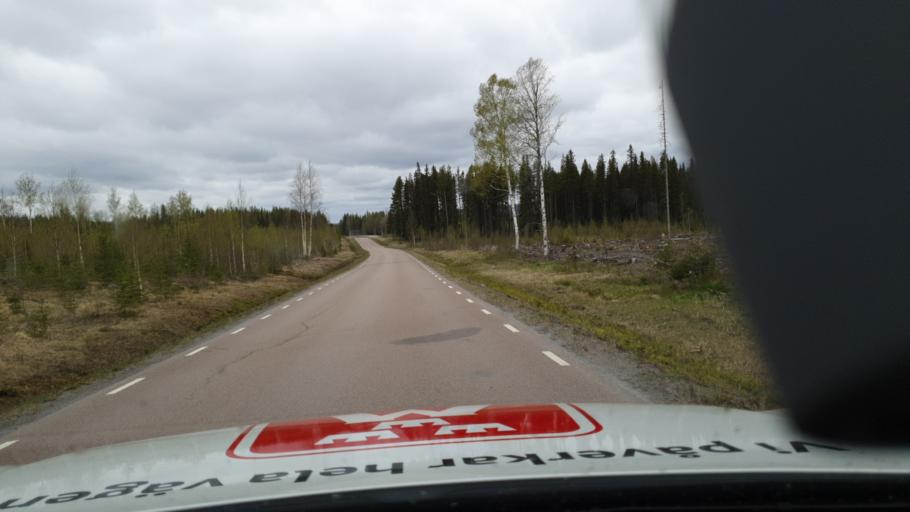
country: SE
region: Jaemtland
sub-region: OEstersunds Kommun
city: Lit
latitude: 63.3063
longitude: 14.9074
